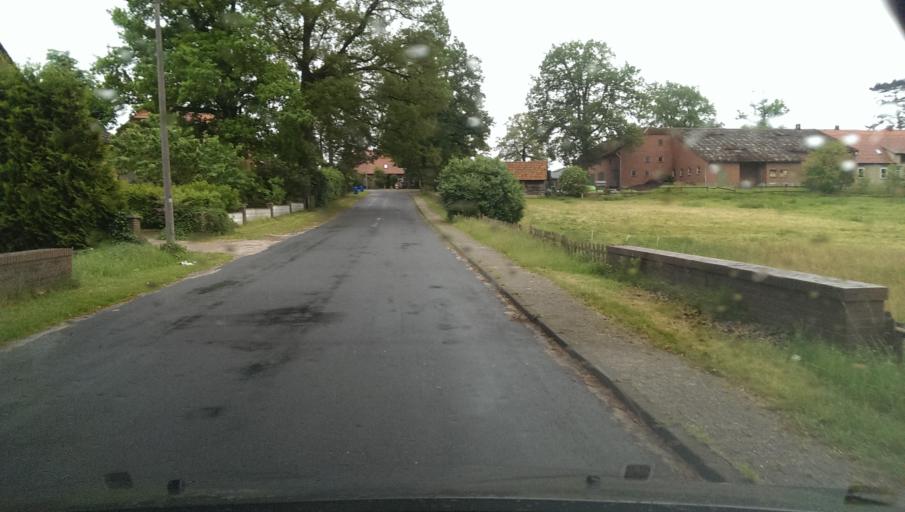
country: DE
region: Lower Saxony
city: Dedelstorf
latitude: 52.7333
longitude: 10.5160
